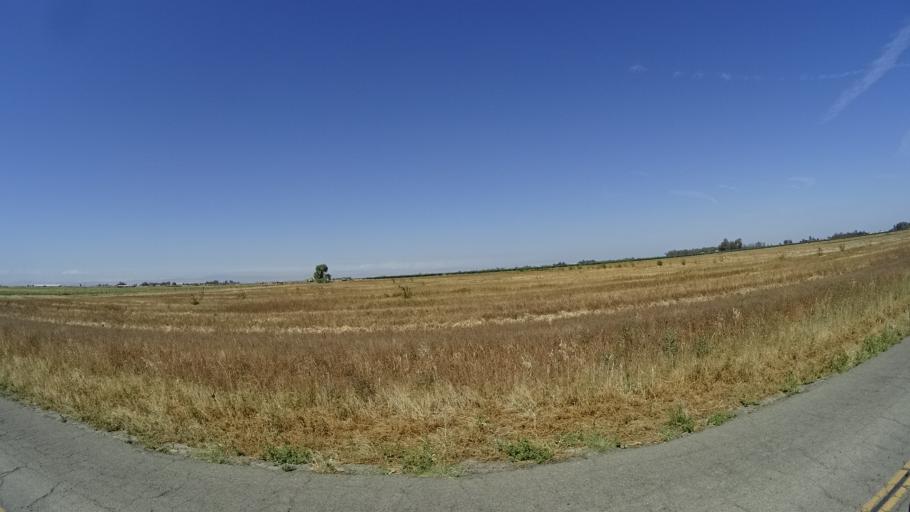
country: US
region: California
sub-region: Kings County
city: Stratford
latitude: 36.1828
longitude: -119.7803
